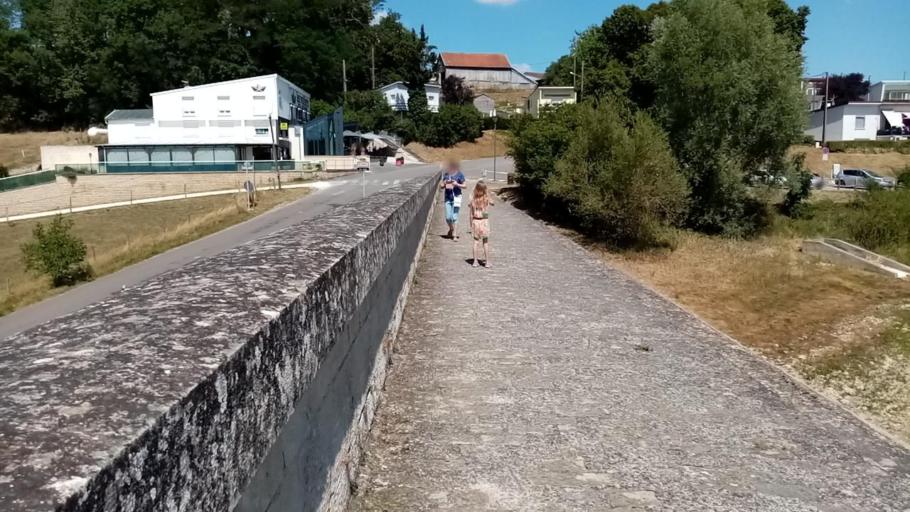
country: FR
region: Champagne-Ardenne
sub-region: Departement de la Haute-Marne
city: Langres
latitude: 47.8680
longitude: 5.3725
